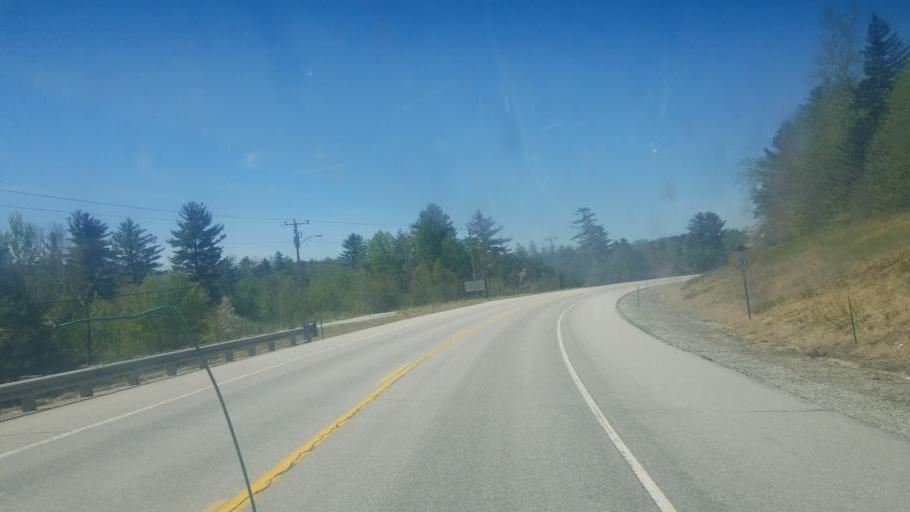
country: US
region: New Hampshire
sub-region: Grafton County
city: Deerfield
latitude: 44.2688
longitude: -71.5264
